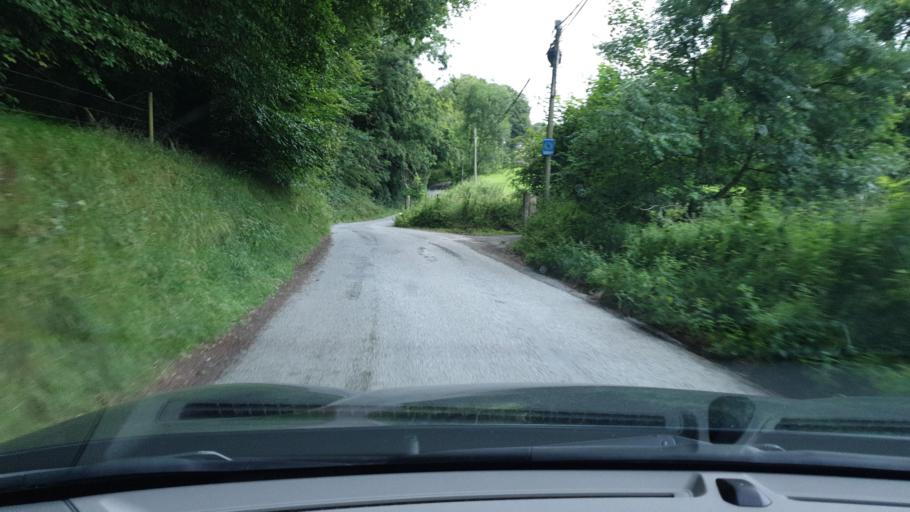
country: IE
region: Leinster
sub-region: South Dublin
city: Rathcoole
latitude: 53.2188
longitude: -6.4835
